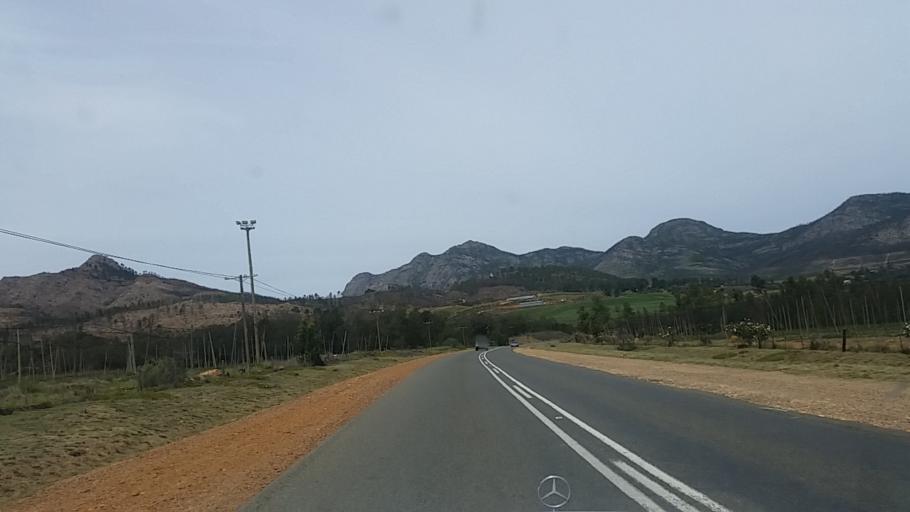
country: ZA
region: Western Cape
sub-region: Eden District Municipality
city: George
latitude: -33.8523
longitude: 22.3581
